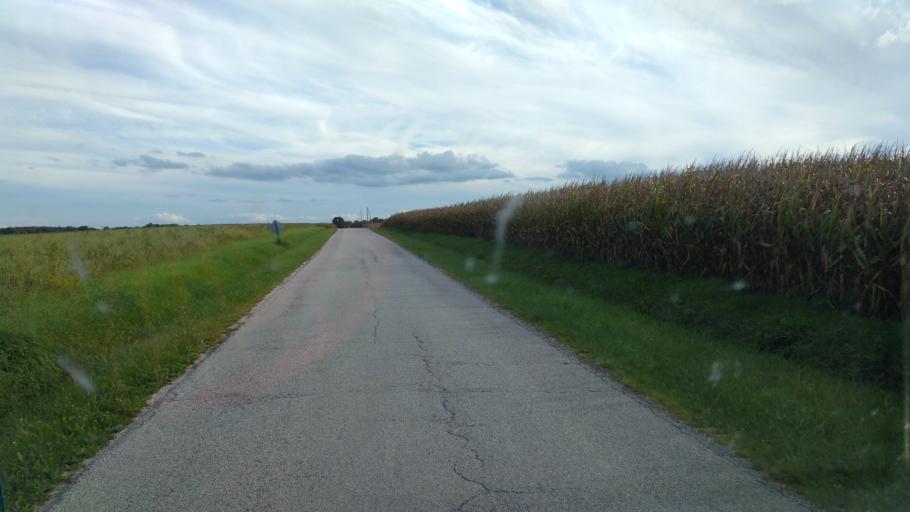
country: US
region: Ohio
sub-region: Crawford County
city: Bucyrus
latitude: 40.8676
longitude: -82.9163
